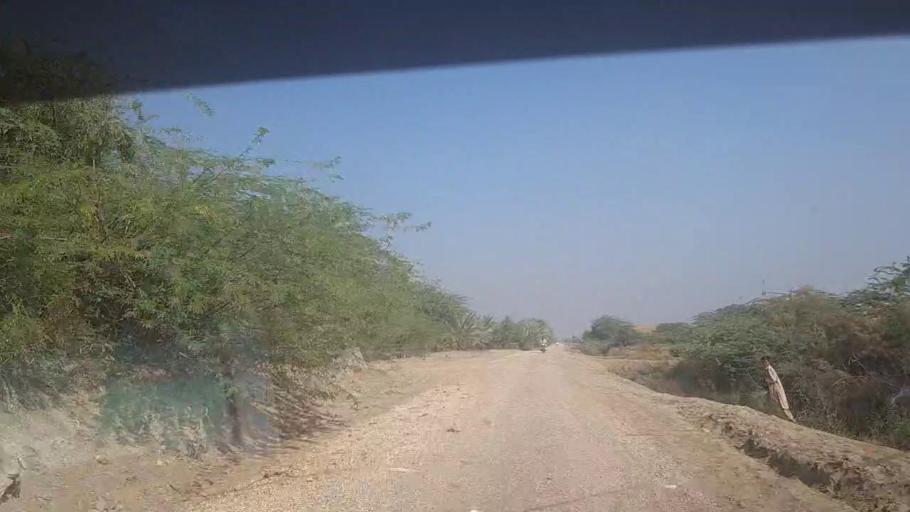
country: PK
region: Sindh
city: Khairpur
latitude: 27.4597
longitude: 68.7281
